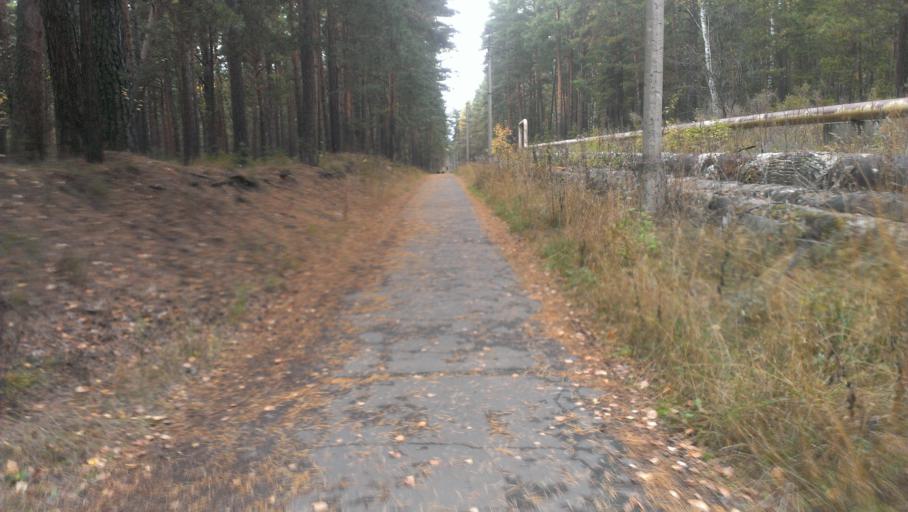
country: RU
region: Altai Krai
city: Yuzhnyy
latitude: 53.2655
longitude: 83.6846
